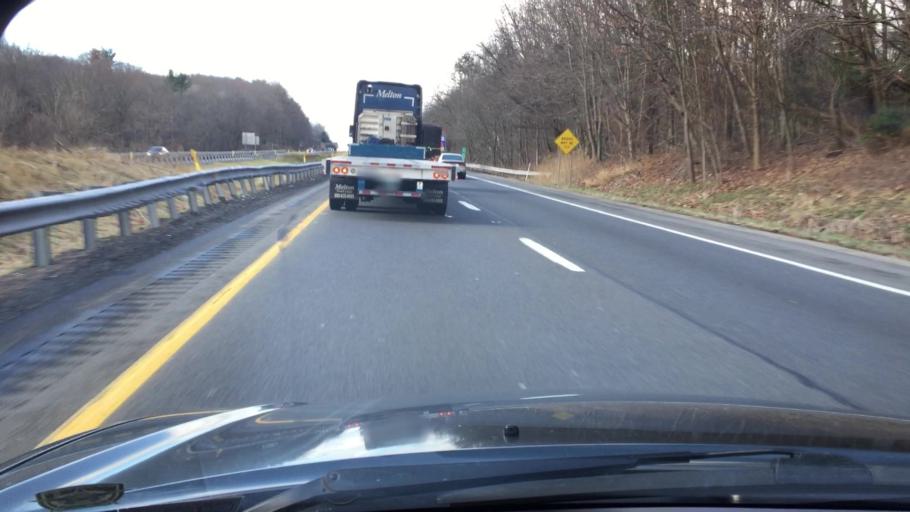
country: US
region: Pennsylvania
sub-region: Monroe County
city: Arlington Heights
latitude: 40.9889
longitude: -75.2418
